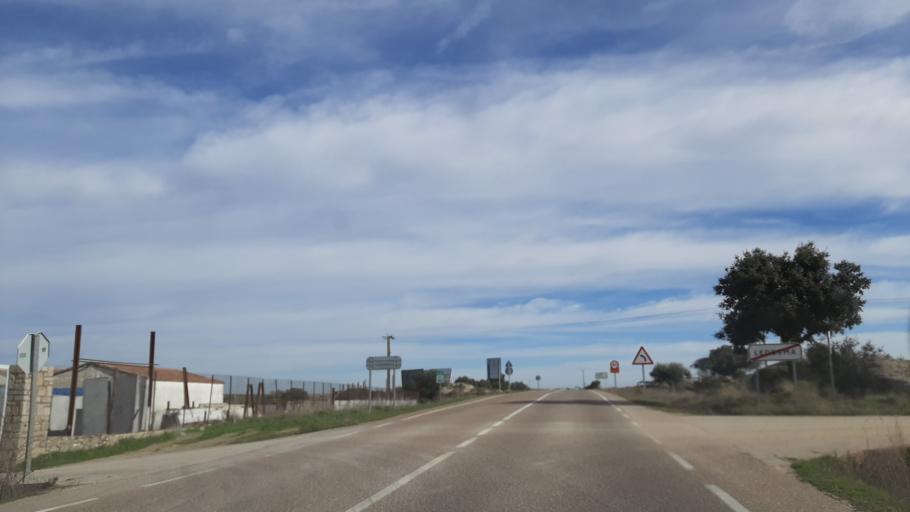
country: ES
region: Castille and Leon
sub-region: Provincia de Salamanca
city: Ledesma
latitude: 41.0916
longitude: -5.9910
